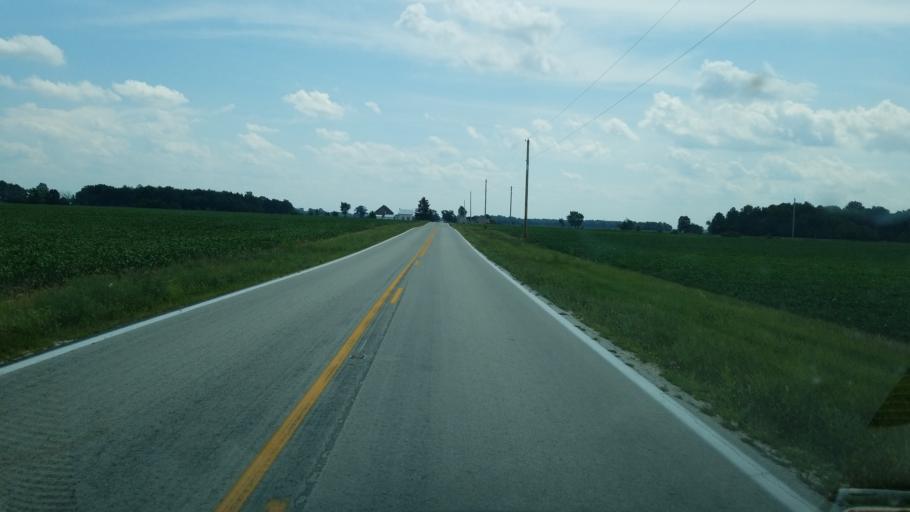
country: US
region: Ohio
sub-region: Wyandot County
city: Carey
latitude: 40.9320
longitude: -83.4672
